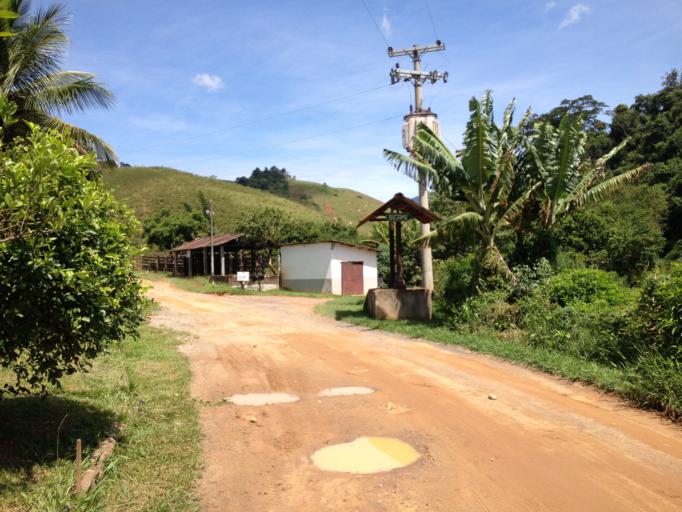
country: BR
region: Rio de Janeiro
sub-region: Barra Do Pirai
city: Barra do Pirai
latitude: -22.3057
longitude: -43.9544
